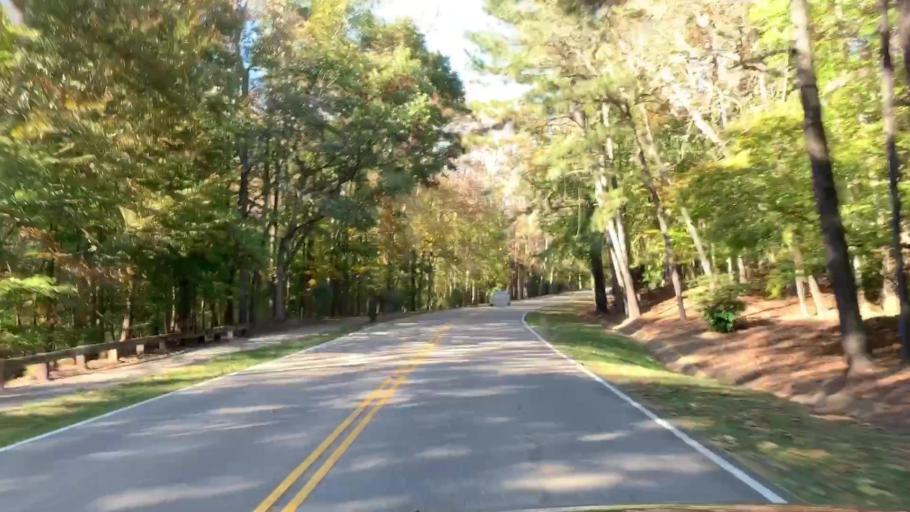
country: US
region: Virginia
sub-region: City of Williamsburg
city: Williamsburg
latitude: 37.2377
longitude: -76.6811
